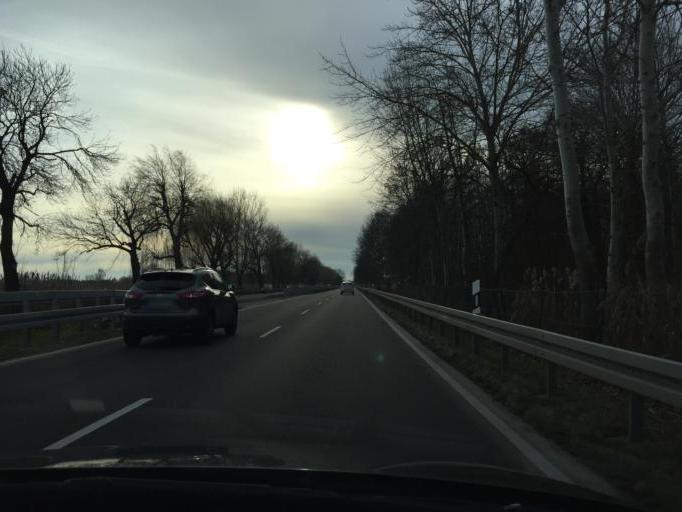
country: DE
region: Brandenburg
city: Peitz
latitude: 51.8375
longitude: 14.3875
